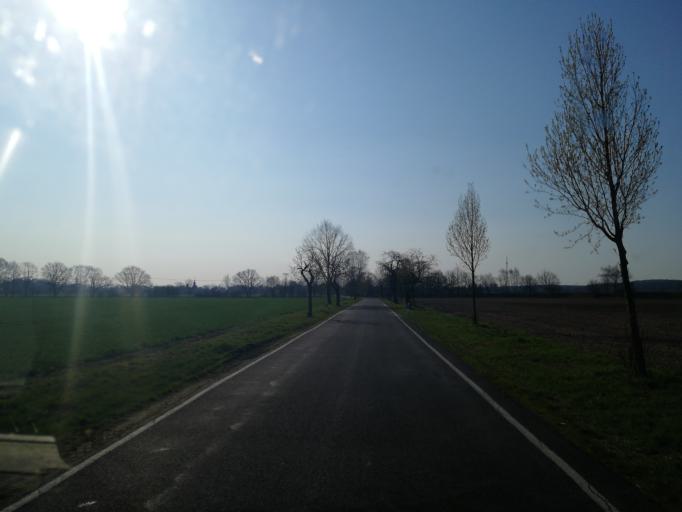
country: DE
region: Brandenburg
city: Drahnsdorf
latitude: 51.8609
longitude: 13.5950
